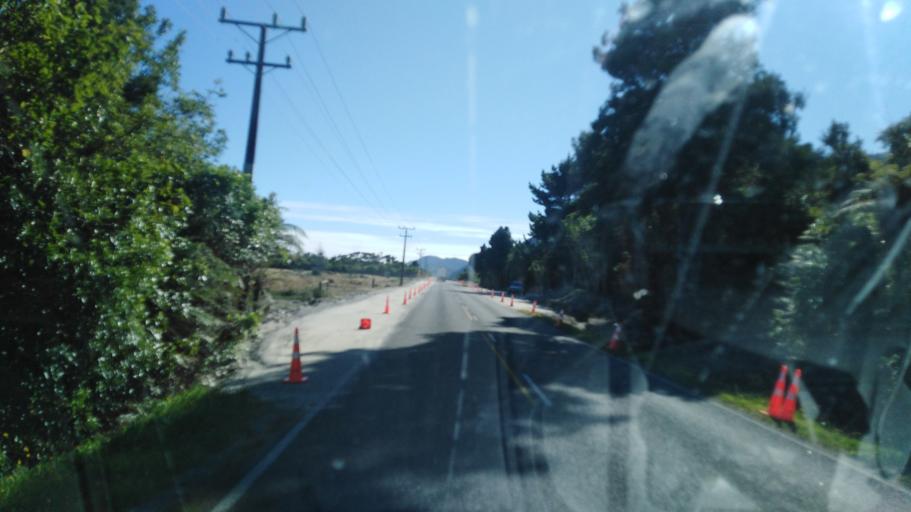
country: NZ
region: West Coast
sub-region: Buller District
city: Westport
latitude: -41.6685
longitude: 171.8076
